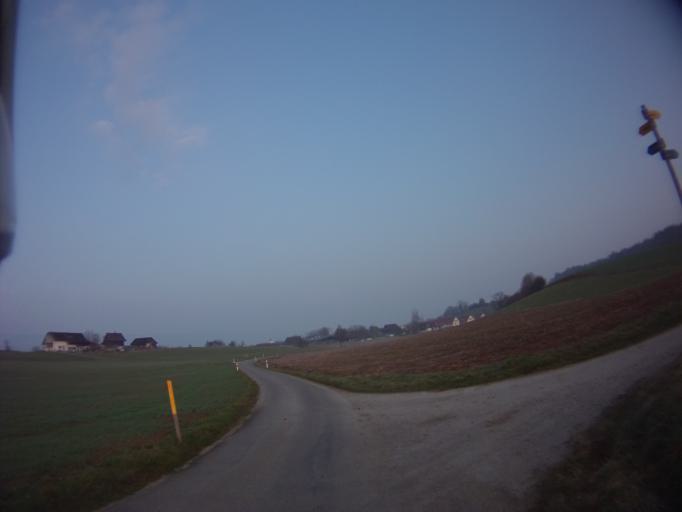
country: CH
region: Zurich
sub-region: Bezirk Affoltern
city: Knonau
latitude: 47.2321
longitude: 8.4372
